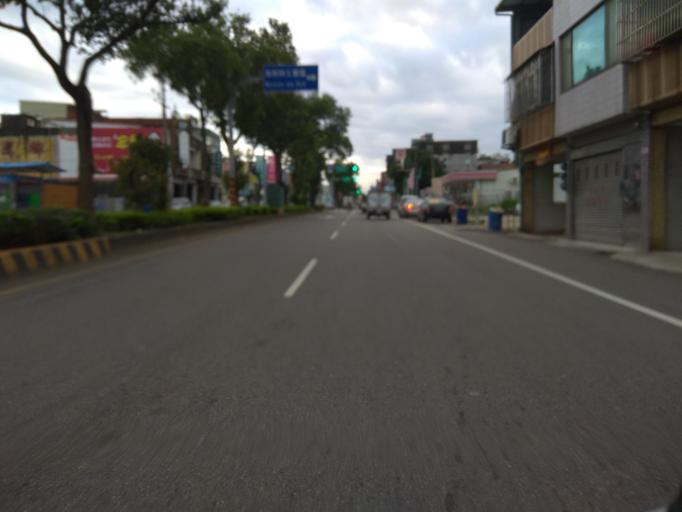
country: TW
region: Taiwan
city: Daxi
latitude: 24.8892
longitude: 121.2126
